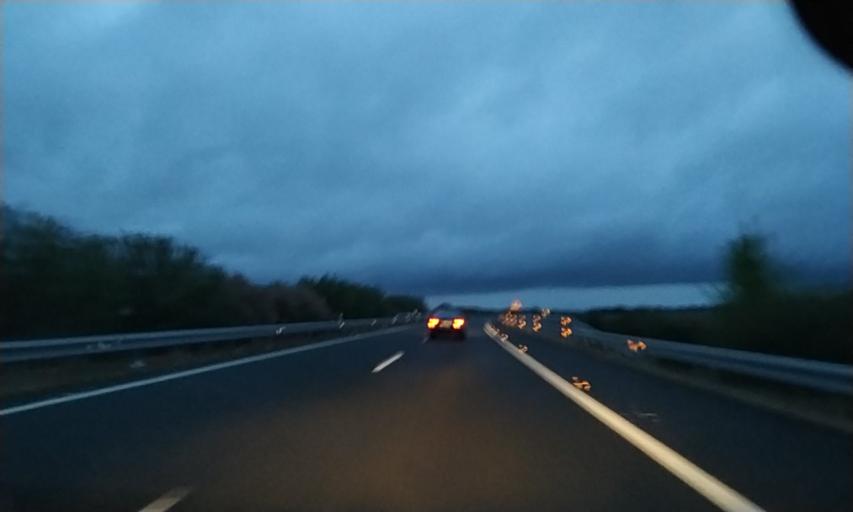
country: ES
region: Extremadura
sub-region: Provincia de Caceres
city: Aldea del Cano
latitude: 39.2884
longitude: -6.3304
